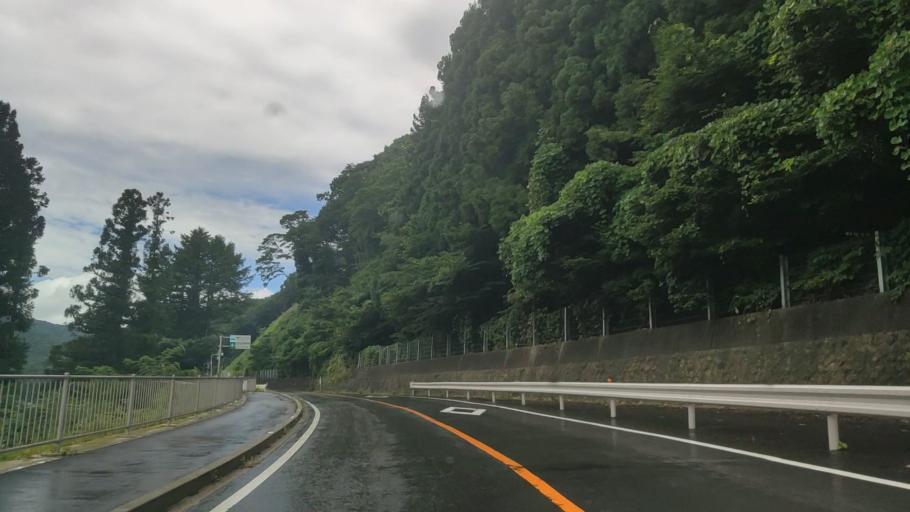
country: JP
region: Gunma
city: Numata
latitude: 36.7620
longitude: 139.2288
